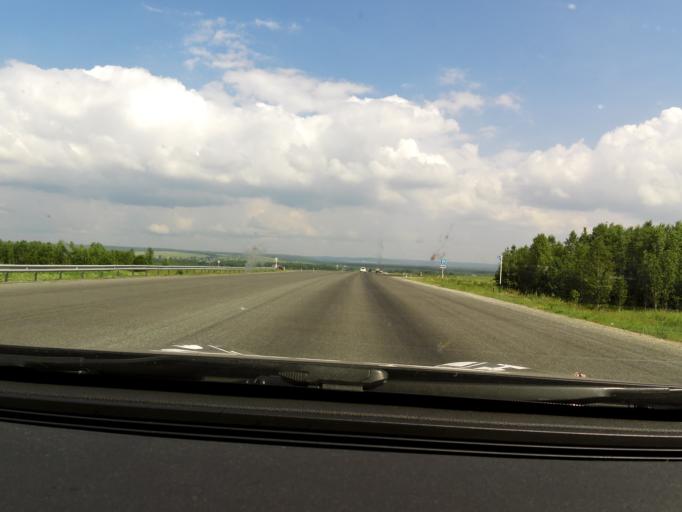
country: RU
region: Sverdlovsk
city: Ufimskiy
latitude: 56.7734
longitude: 58.0493
